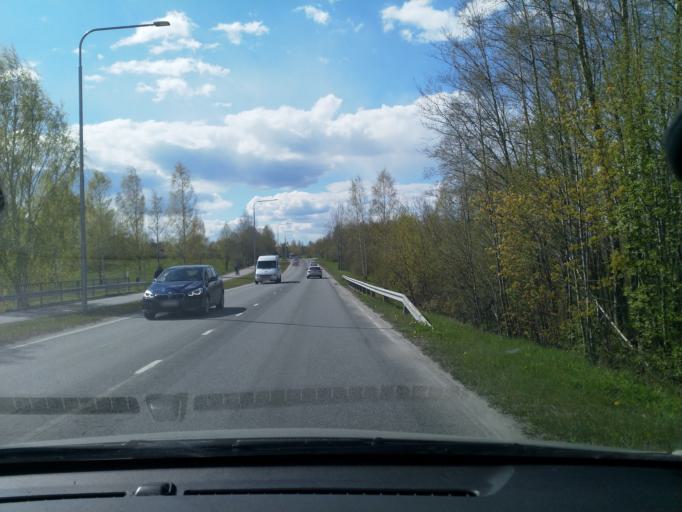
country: FI
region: Pirkanmaa
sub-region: Tampere
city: Tampere
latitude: 61.4797
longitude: 23.8207
